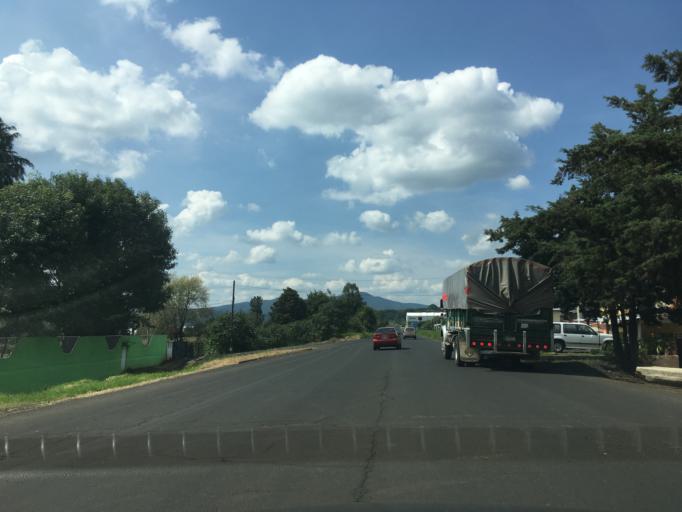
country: MX
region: Michoacan
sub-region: Tingueindin
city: Tingueindin
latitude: 19.7740
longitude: -102.5004
